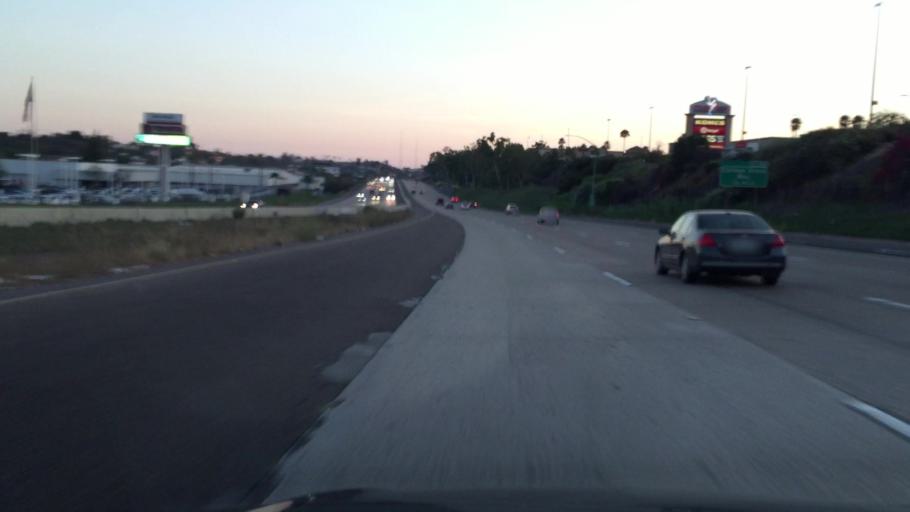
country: US
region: California
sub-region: San Diego County
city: Lemon Grove
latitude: 32.7409
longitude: -117.0522
